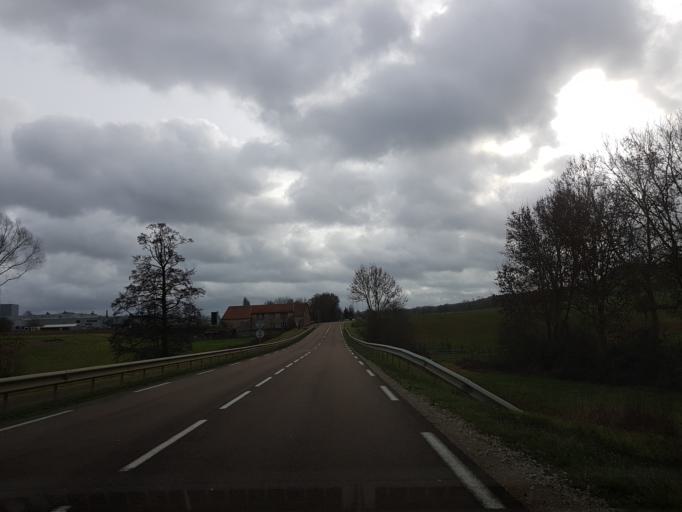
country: FR
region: Champagne-Ardenne
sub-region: Departement de la Haute-Marne
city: Langres
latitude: 47.8613
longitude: 5.3434
